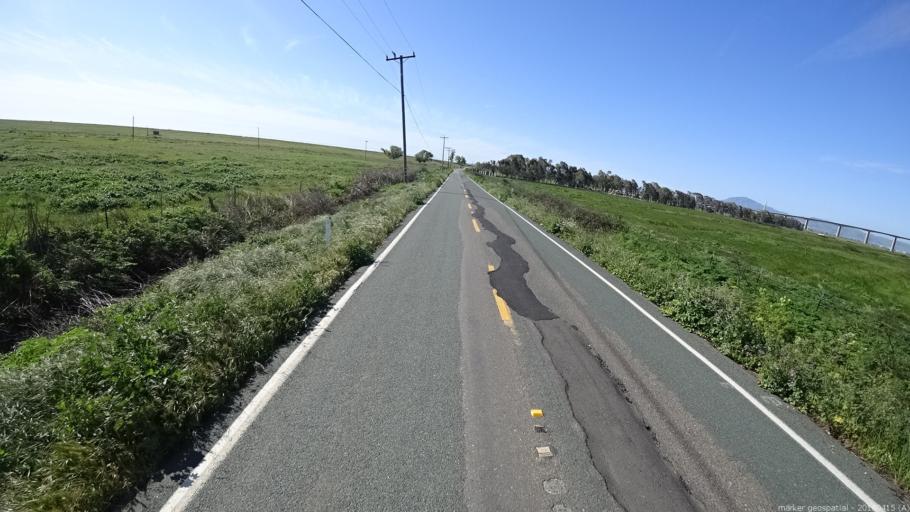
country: US
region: California
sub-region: Contra Costa County
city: Oakley
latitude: 38.0373
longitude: -121.7362
